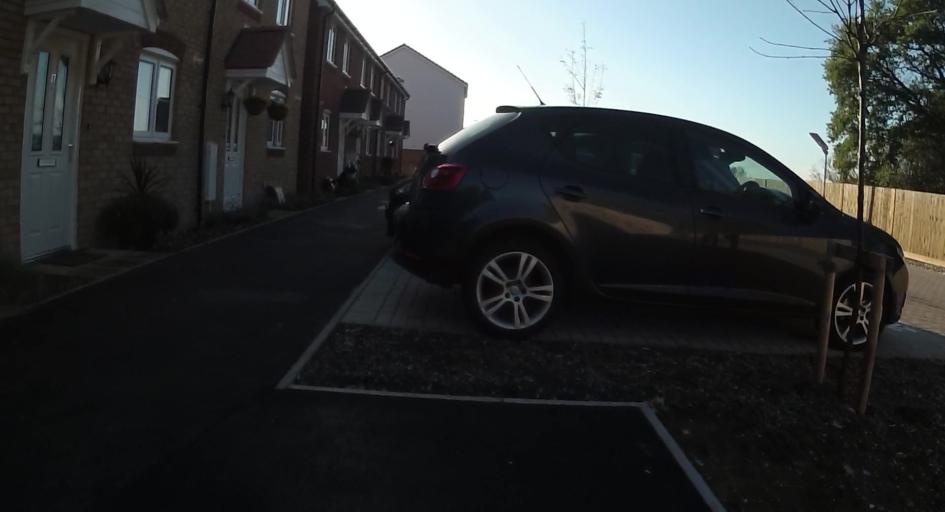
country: GB
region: England
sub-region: Wokingham
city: Winnersh
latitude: 51.4295
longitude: -0.8883
